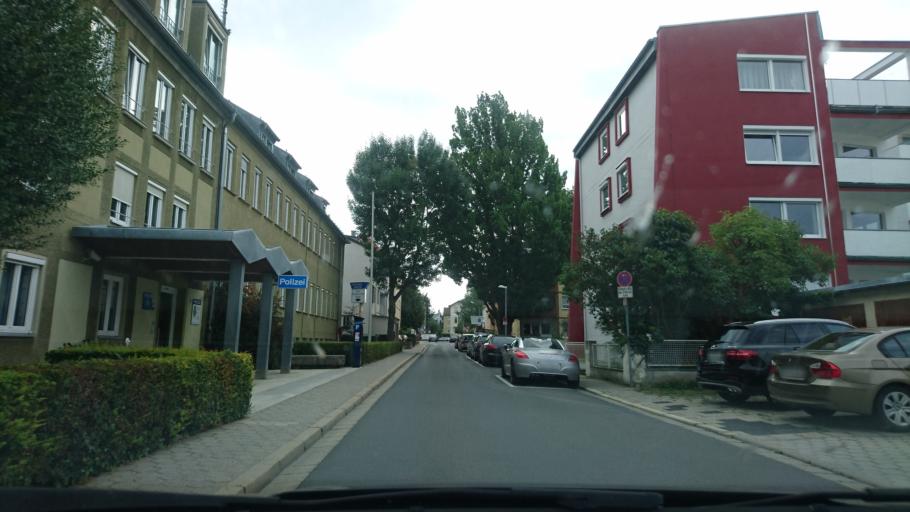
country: DE
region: Bavaria
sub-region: Upper Franconia
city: Bayreuth
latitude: 49.9431
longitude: 11.5815
